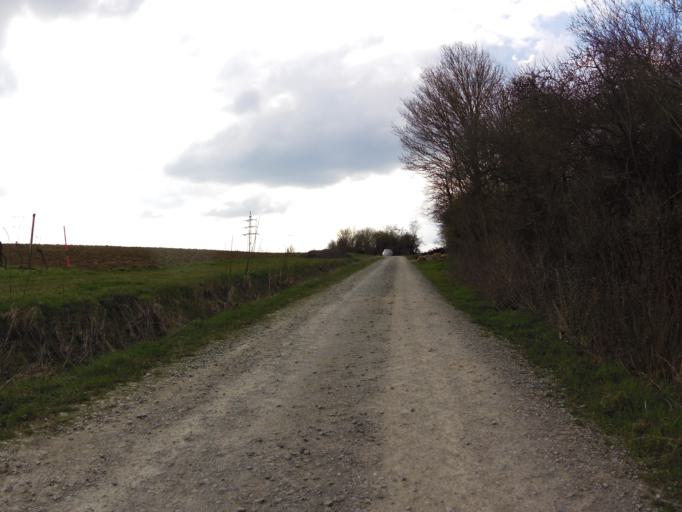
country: DE
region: Bavaria
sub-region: Regierungsbezirk Unterfranken
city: Buchbrunn
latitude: 49.7380
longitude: 10.1167
